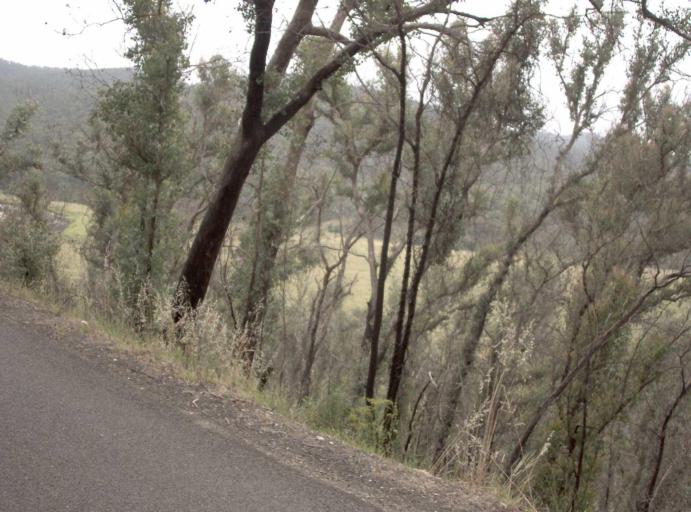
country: AU
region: Victoria
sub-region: Wellington
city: Heyfield
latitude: -37.8121
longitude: 146.6723
